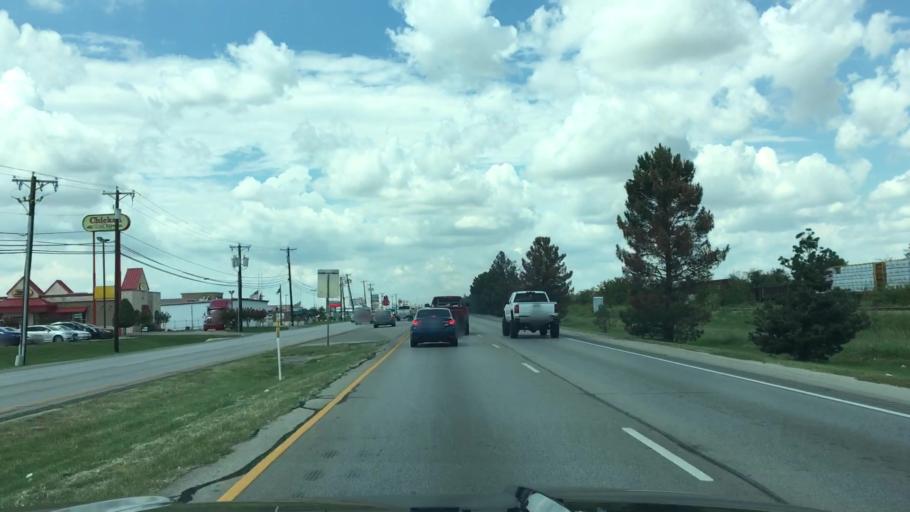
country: US
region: Texas
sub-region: Tarrant County
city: Saginaw
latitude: 32.8732
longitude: -97.3750
